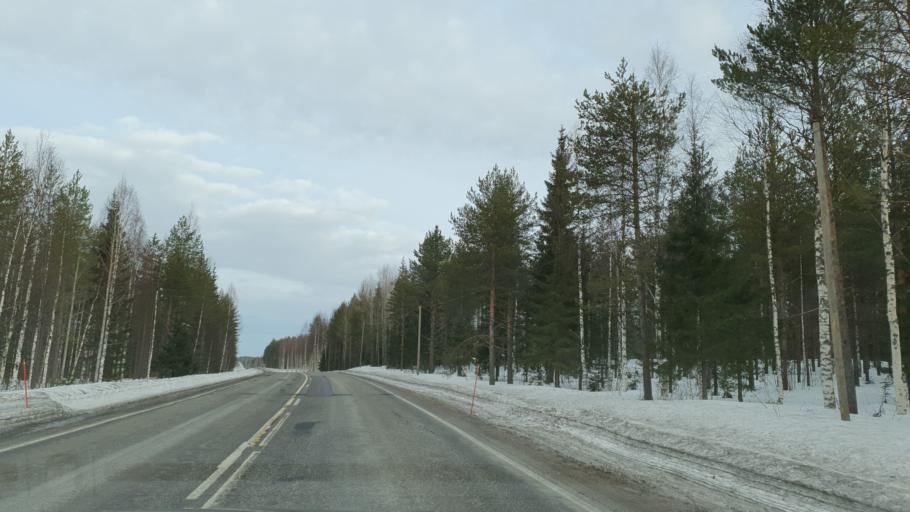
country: FI
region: Kainuu
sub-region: Kajaani
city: Vuokatti
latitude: 64.1986
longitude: 28.1677
